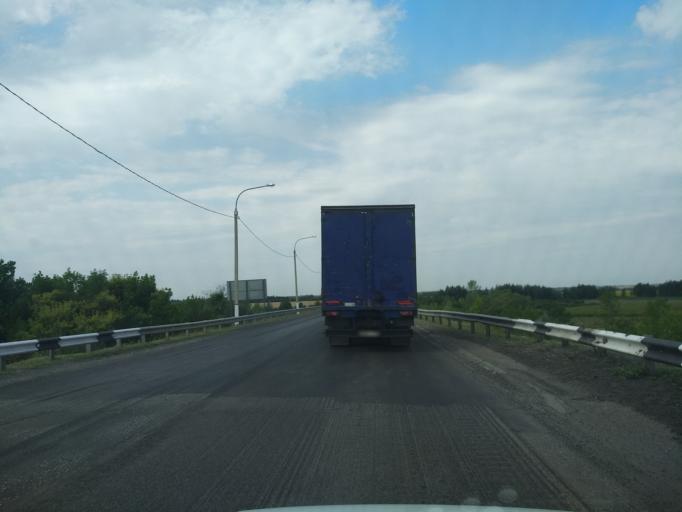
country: RU
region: Voronezj
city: Pereleshino
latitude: 51.7616
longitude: 40.1261
